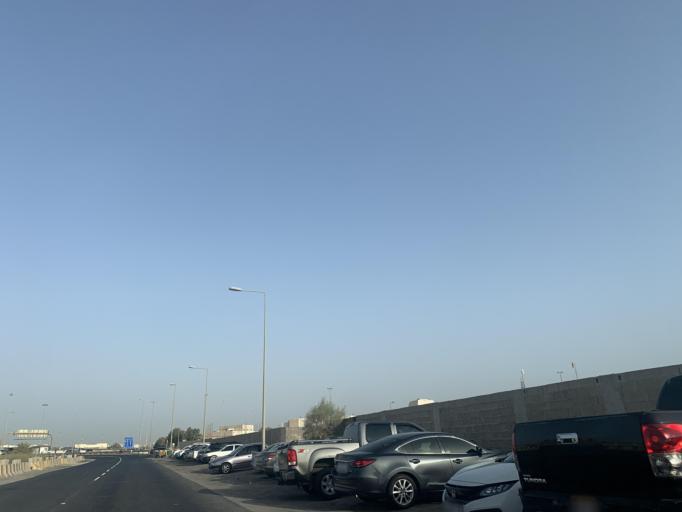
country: BH
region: Central Governorate
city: Madinat Hamad
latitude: 26.1738
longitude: 50.4607
